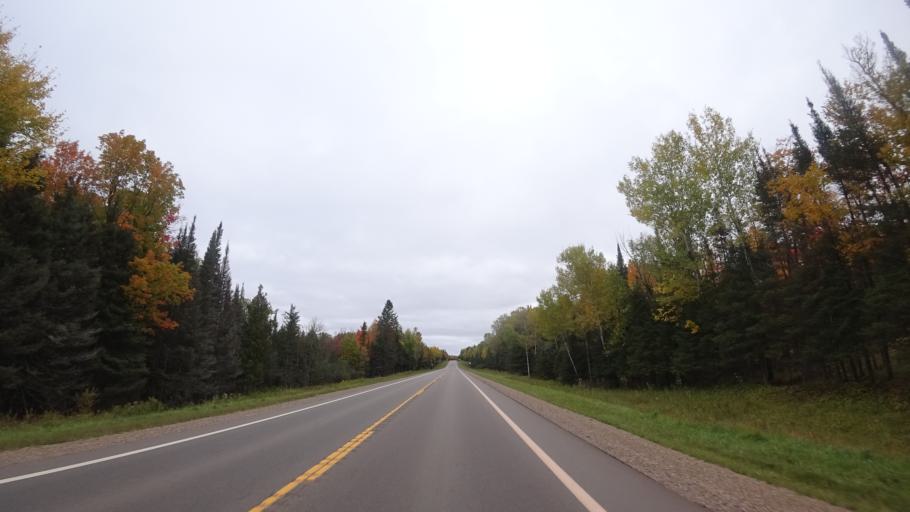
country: US
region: Michigan
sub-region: Iron County
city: Crystal Falls
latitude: 46.1561
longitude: -88.0838
